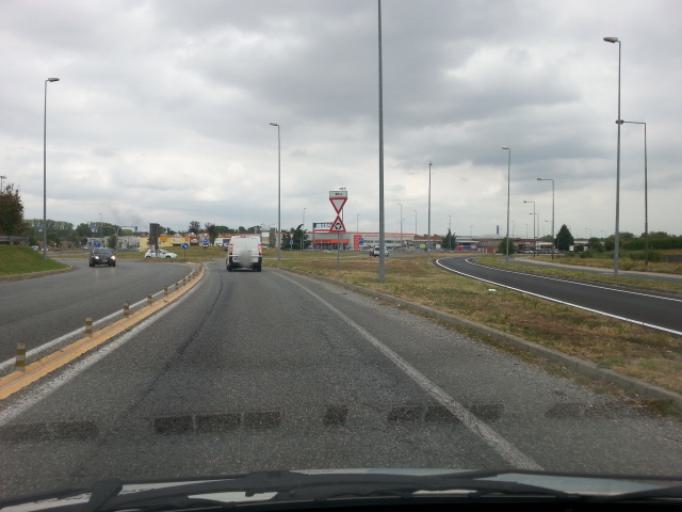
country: IT
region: Piedmont
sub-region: Provincia di Torino
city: Pasta
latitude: 45.0098
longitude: 7.5557
